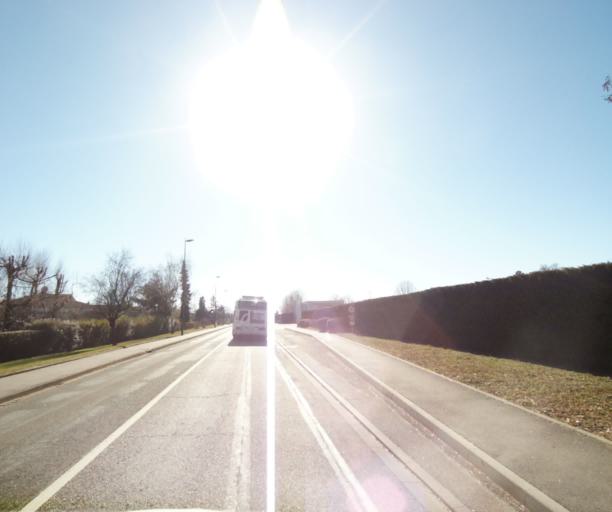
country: FR
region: Lorraine
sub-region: Departement de Meurthe-et-Moselle
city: Jarville-la-Malgrange
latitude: 48.6650
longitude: 6.2079
